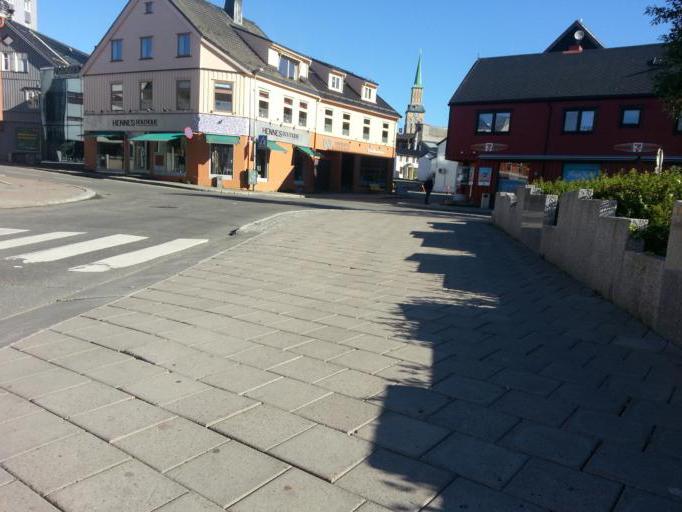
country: NO
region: Troms
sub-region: Tromso
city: Tromso
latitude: 69.6473
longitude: 18.9546
